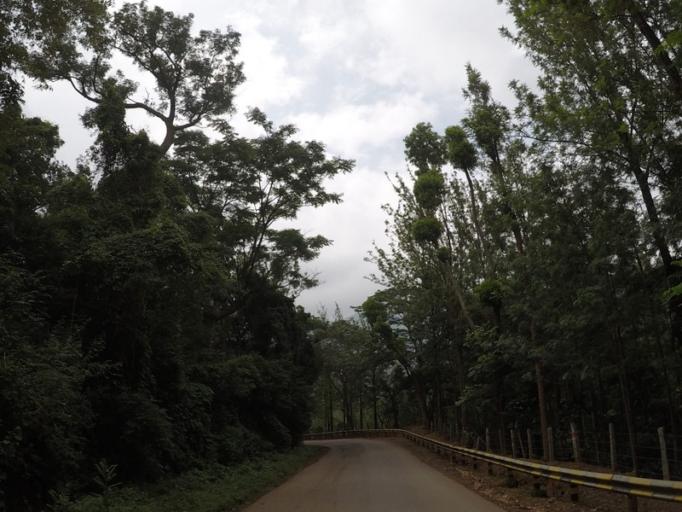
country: IN
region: Karnataka
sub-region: Chikmagalur
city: Chikmagalur
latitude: 13.5032
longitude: 75.8013
